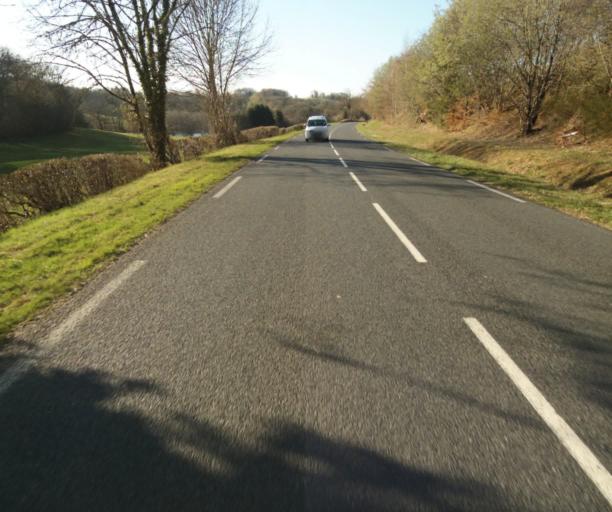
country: FR
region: Limousin
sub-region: Departement de la Correze
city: Seilhac
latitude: 45.3910
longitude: 1.7199
